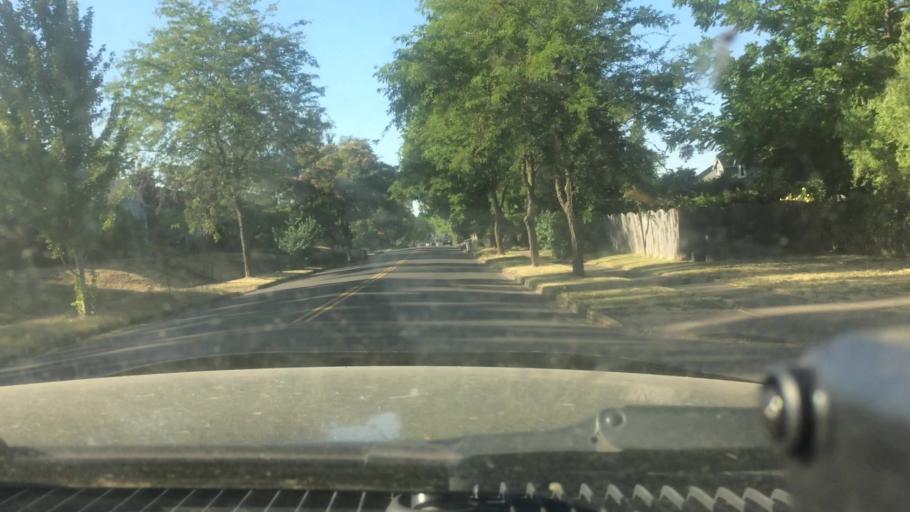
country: US
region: Oregon
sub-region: Lane County
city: Eugene
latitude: 44.0366
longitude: -123.1012
